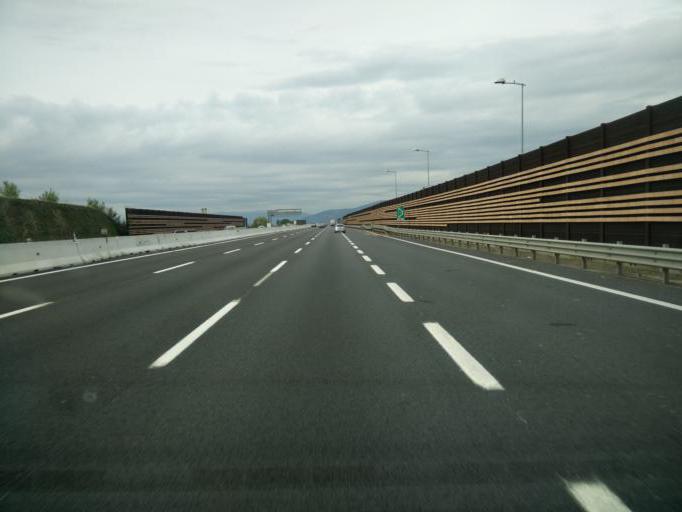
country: IT
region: Tuscany
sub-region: Province of Florence
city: Mantignano-Ugnano
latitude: 43.7800
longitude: 11.1608
